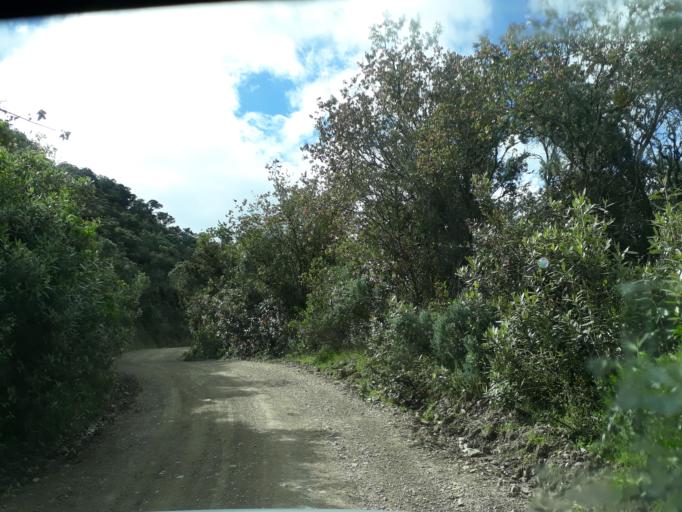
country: CO
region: Cundinamarca
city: La Mesa
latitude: 5.2505
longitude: -73.8945
